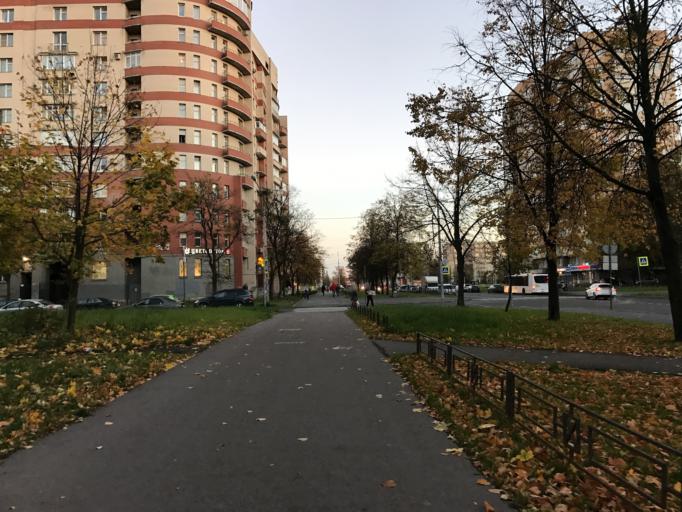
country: RU
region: St.-Petersburg
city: Obukhovo
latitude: 59.8996
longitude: 30.4728
